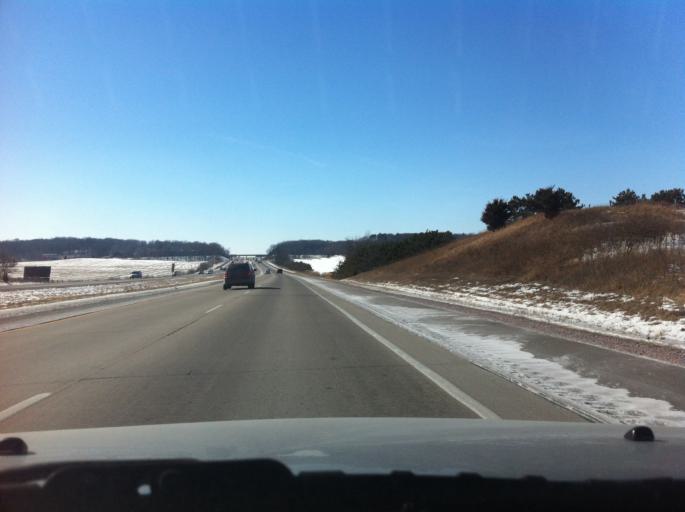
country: US
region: Wisconsin
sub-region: Columbia County
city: Portage
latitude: 43.5386
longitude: -89.5999
